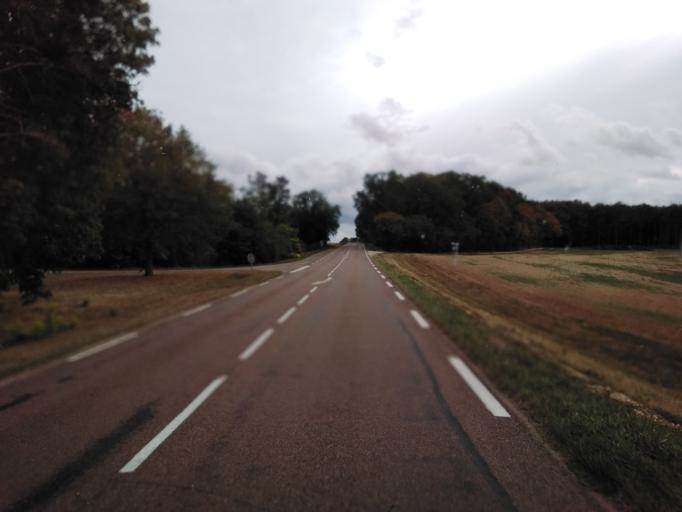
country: FR
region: Champagne-Ardenne
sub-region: Departement de l'Aube
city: Bar-sur-Seine
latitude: 48.1580
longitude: 4.4125
